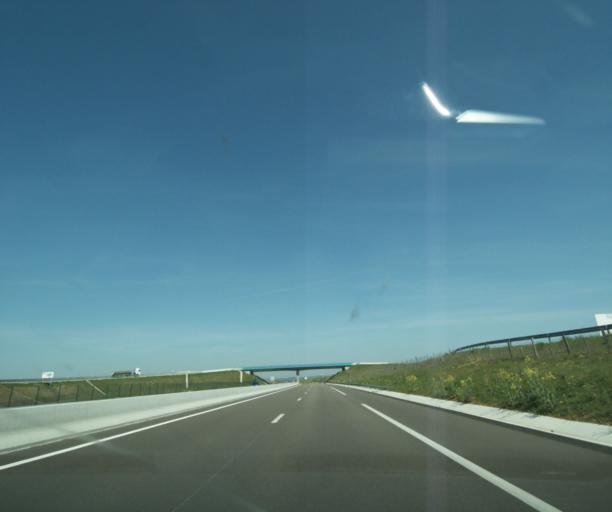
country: FR
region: Bourgogne
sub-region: Departement de la Nievre
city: Saint-Pierre-le-Moutier
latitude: 46.8169
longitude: 3.1241
